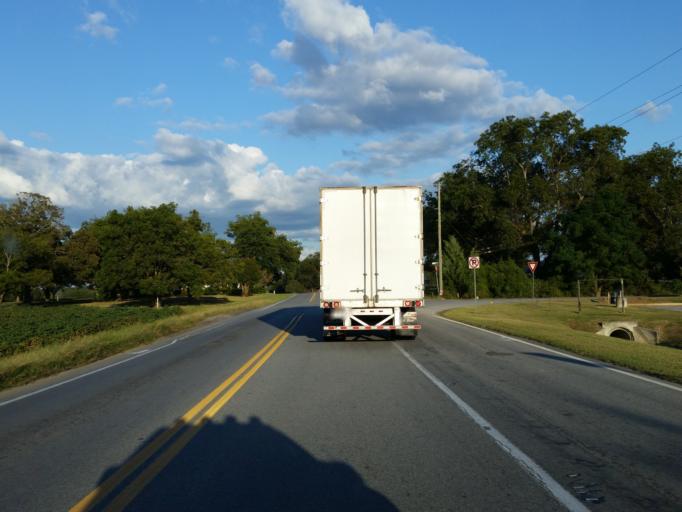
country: US
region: Georgia
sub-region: Dooly County
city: Vienna
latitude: 32.0864
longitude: -83.7597
